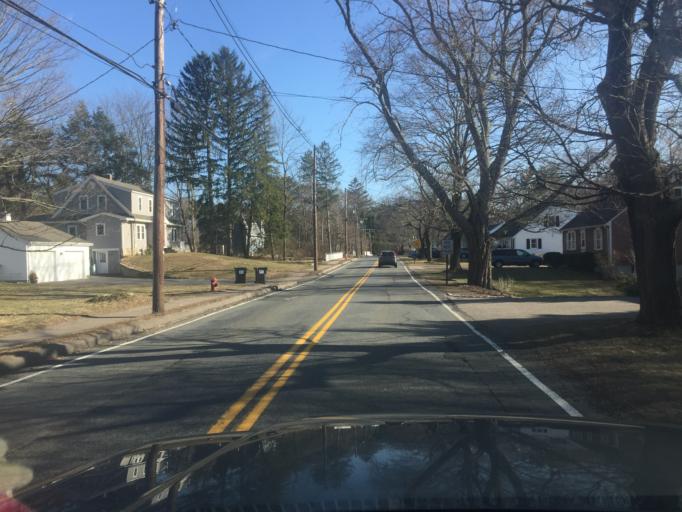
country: US
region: Massachusetts
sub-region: Norfolk County
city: Millis-Clicquot
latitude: 42.1585
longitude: -71.3528
